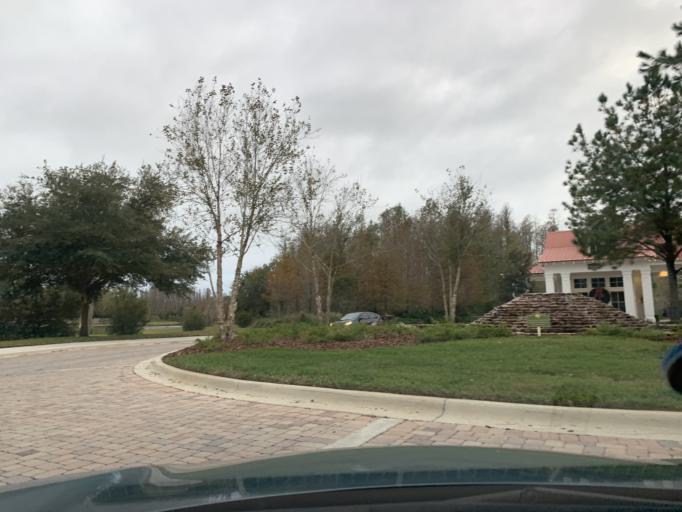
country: US
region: Florida
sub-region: Pasco County
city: Land O' Lakes
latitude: 28.2850
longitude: -82.4876
